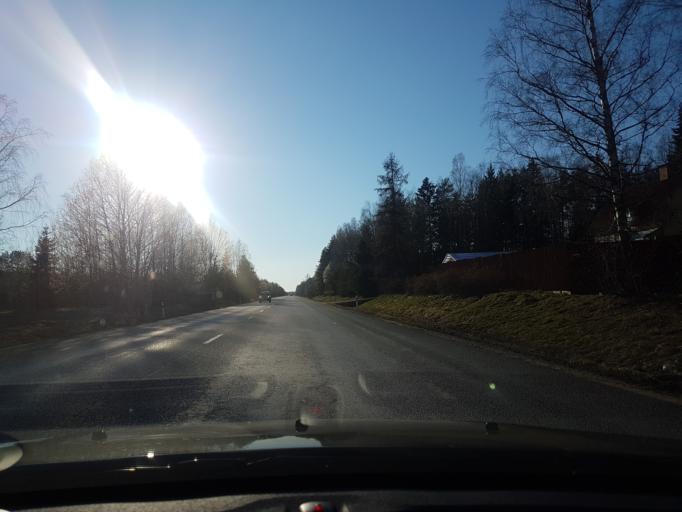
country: SE
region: Uppsala
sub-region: Heby Kommun
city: Morgongava
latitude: 59.8939
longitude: 17.1442
